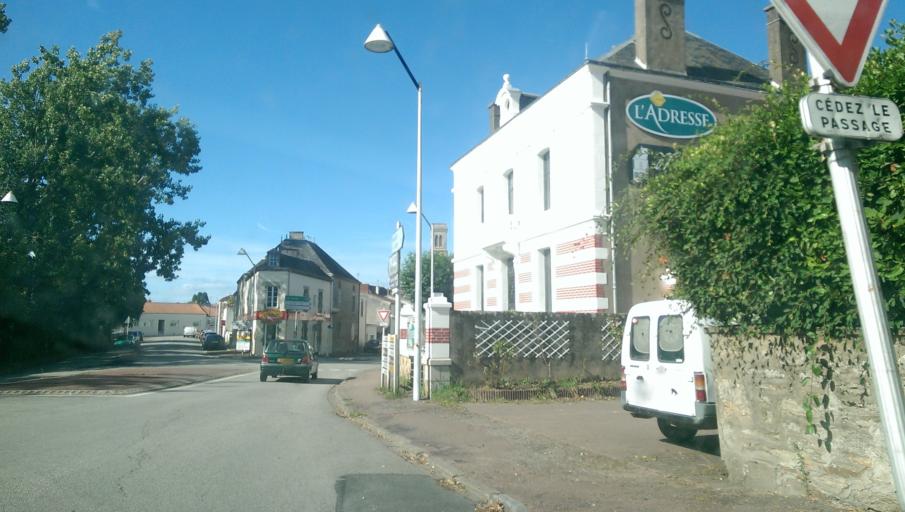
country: FR
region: Pays de la Loire
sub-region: Departement de la Vendee
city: Aizenay
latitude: 46.7376
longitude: -1.6099
